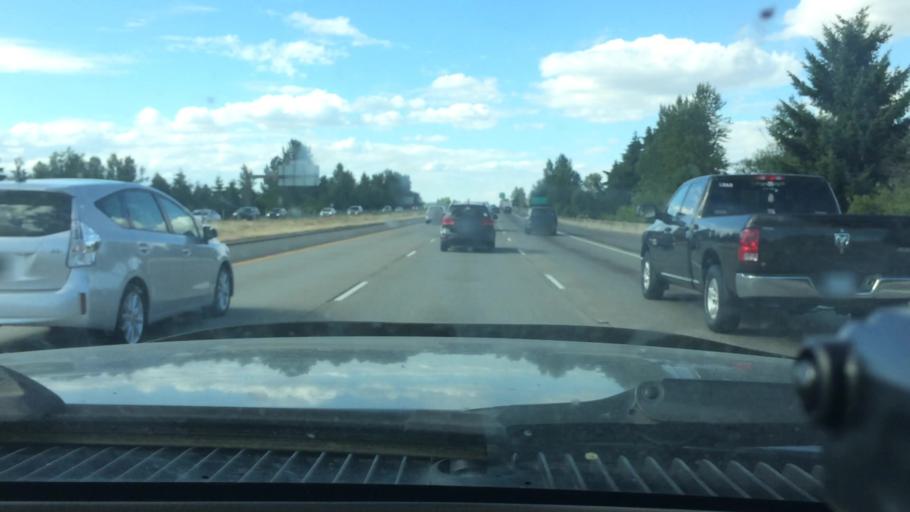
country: US
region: Oregon
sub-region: Marion County
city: Four Corners
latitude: 44.9235
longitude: -122.9902
